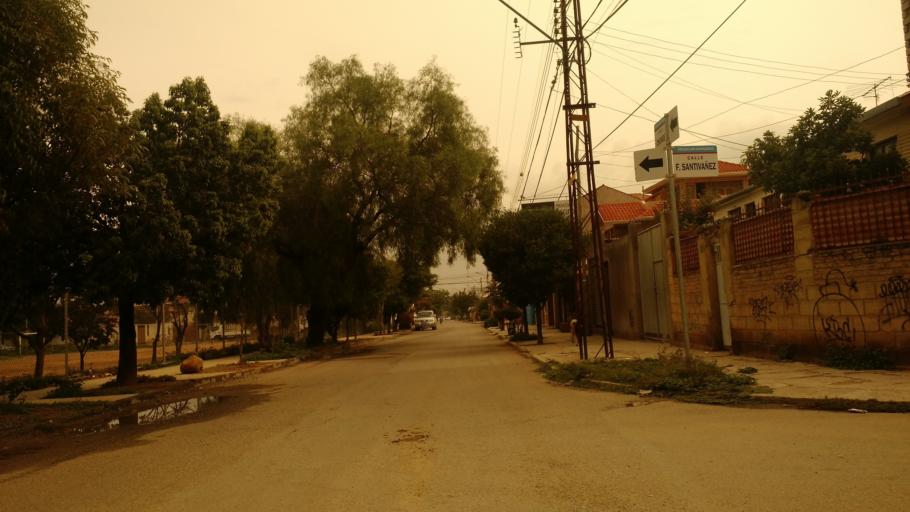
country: BO
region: Cochabamba
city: Cochabamba
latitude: -17.4244
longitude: -66.1558
